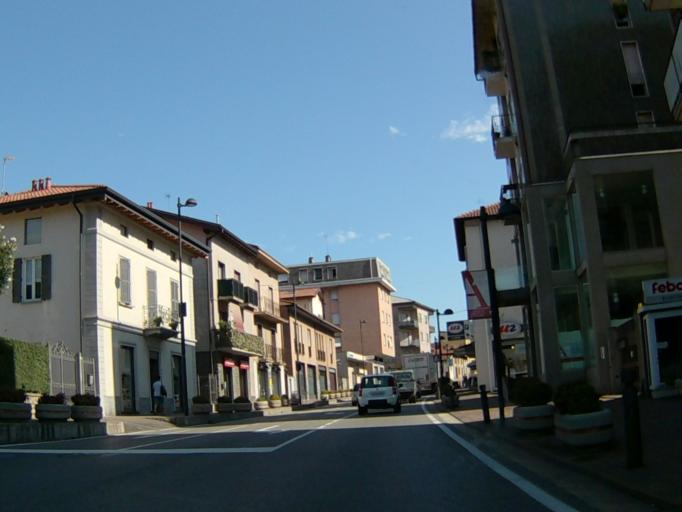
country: IT
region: Lombardy
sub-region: Provincia di Lecco
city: Calolziocorte
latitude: 45.8017
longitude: 9.4305
